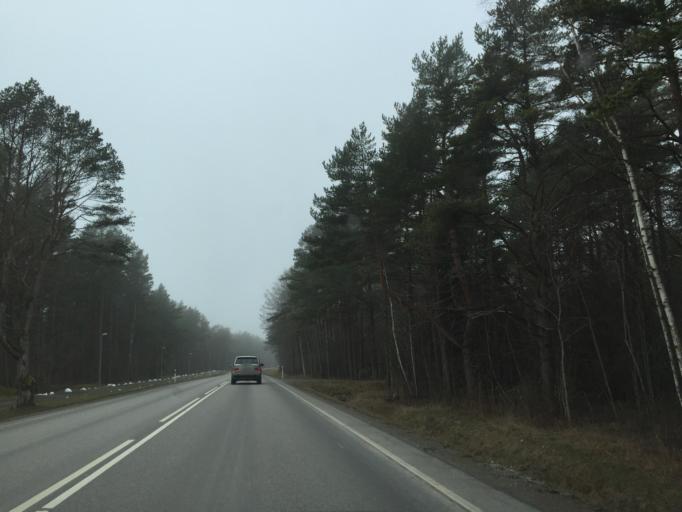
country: EE
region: Saare
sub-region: Kuressaare linn
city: Kuressaare
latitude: 58.2201
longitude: 22.3444
